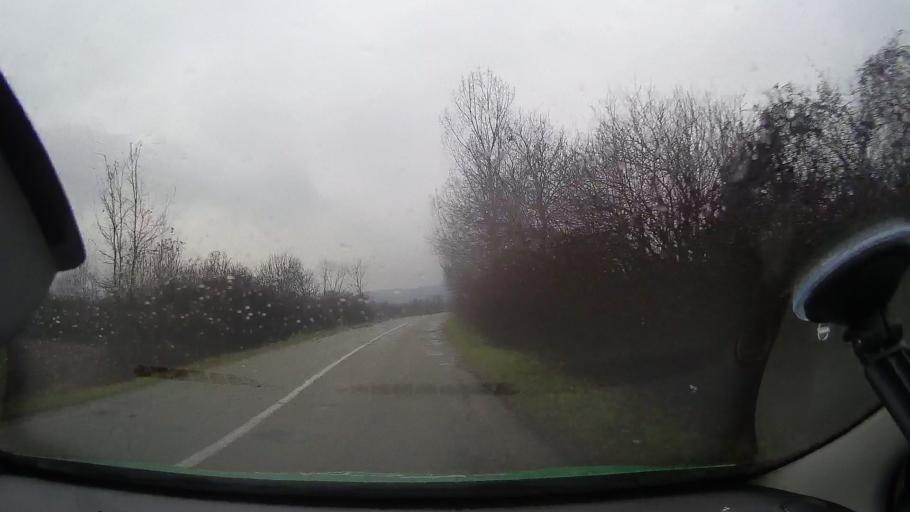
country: RO
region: Arad
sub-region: Comuna Ignesti
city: Ignesti
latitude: 46.3934
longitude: 22.1789
